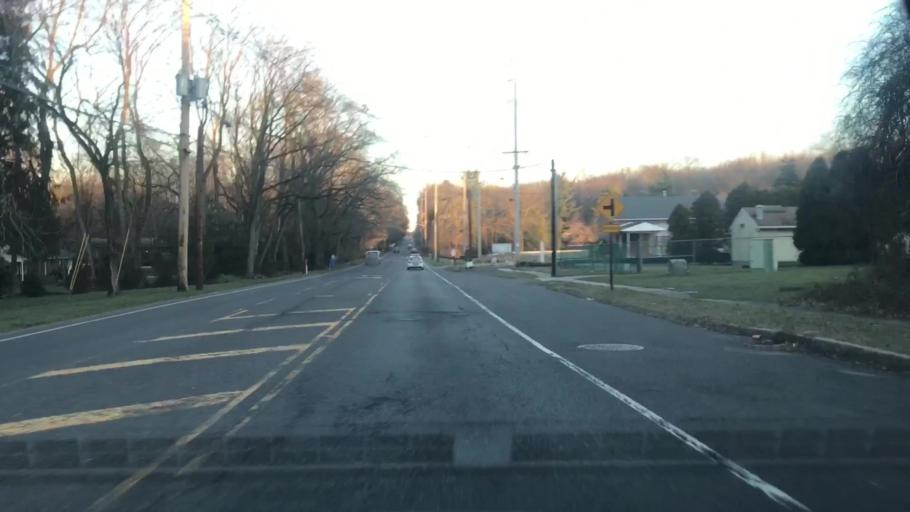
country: US
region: New Jersey
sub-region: Burlington County
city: Burlington
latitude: 40.0499
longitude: -74.8637
